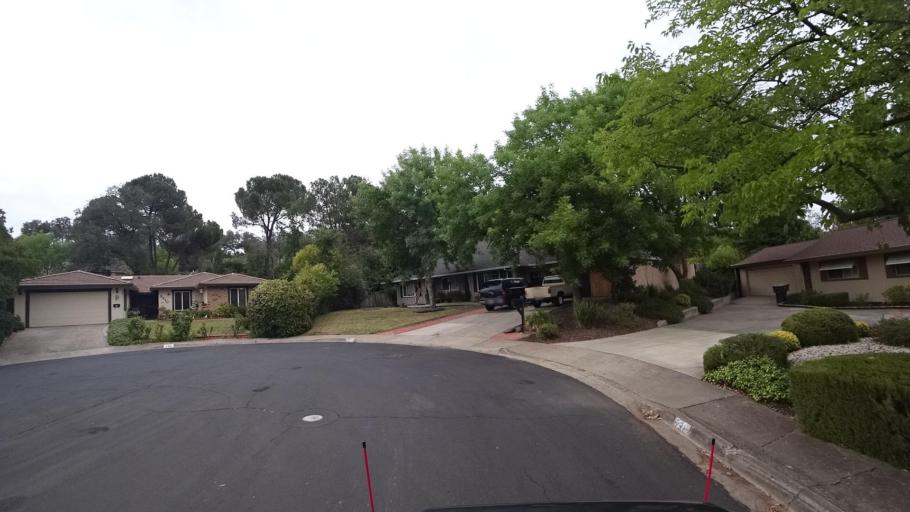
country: US
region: California
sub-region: Placer County
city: Rocklin
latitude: 38.7905
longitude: -121.2523
